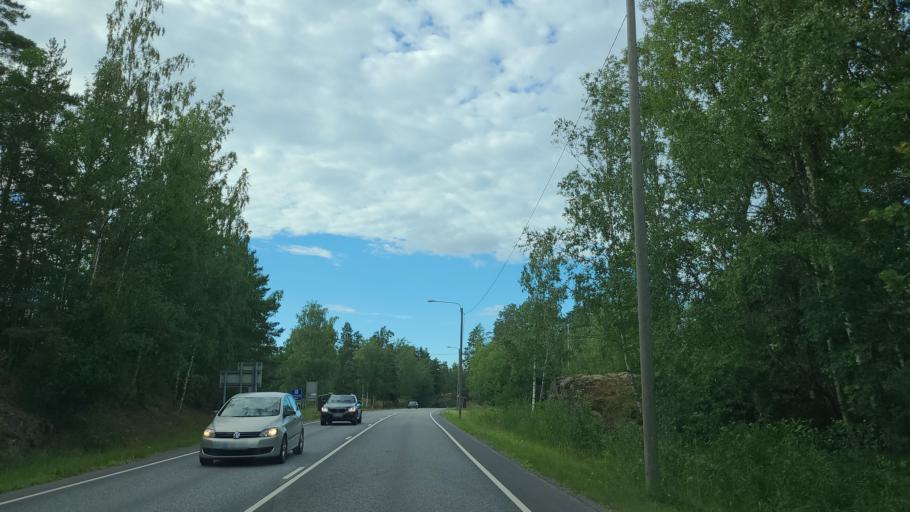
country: FI
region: Varsinais-Suomi
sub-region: Turku
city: Rymaettylae
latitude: 60.4166
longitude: 21.8972
